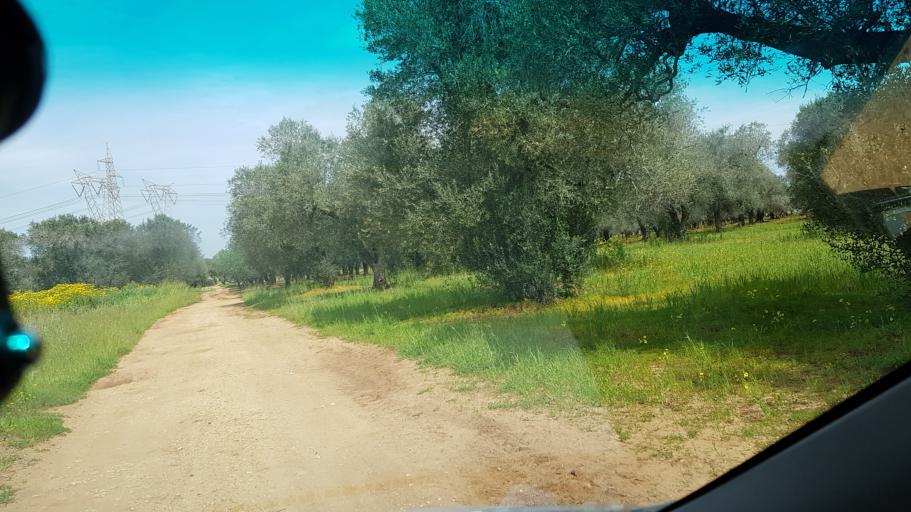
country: IT
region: Apulia
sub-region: Provincia di Brindisi
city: Mesagne
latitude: 40.6038
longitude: 17.8539
